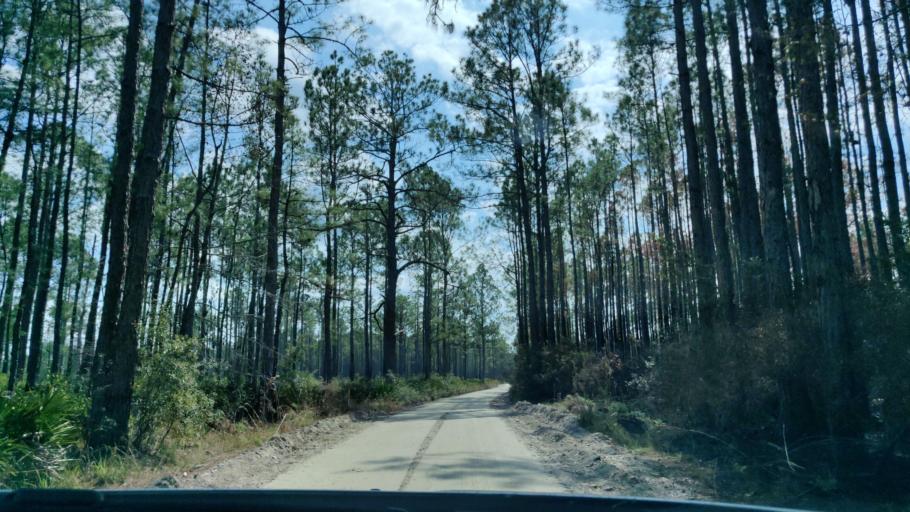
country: US
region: Florida
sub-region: Clay County
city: Middleburg
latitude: 30.1643
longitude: -81.9482
